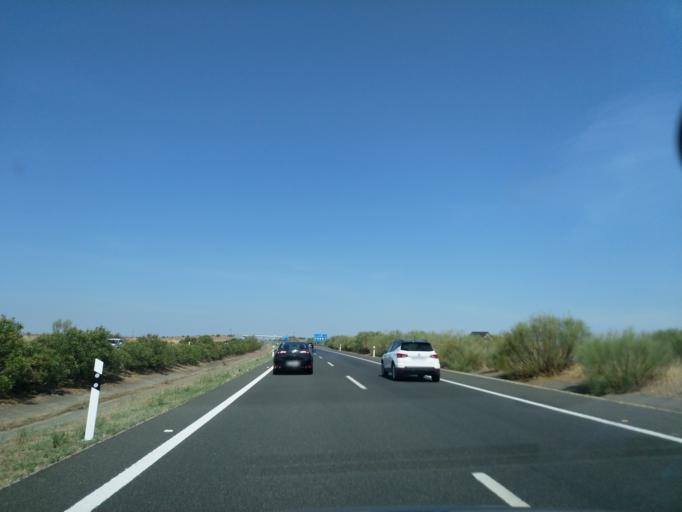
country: ES
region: Extremadura
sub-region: Provincia de Caceres
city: Aldea del Cano
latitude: 39.2773
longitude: -6.3242
